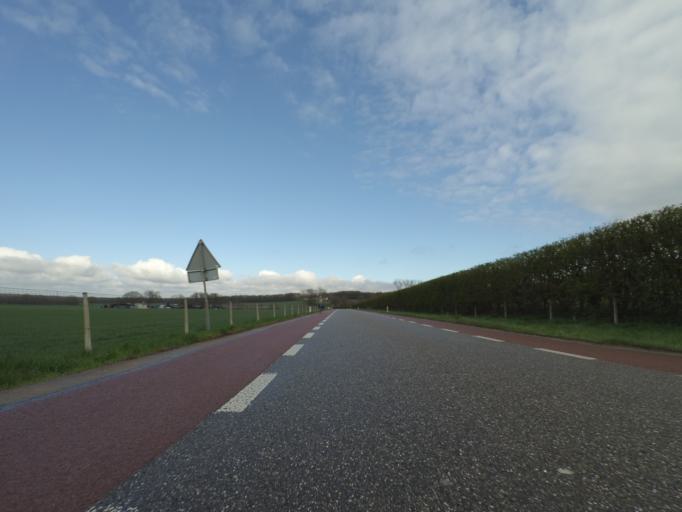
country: NL
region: Gelderland
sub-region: Gemeente Arnhem
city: Hoogkamp
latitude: 52.0635
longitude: 5.8951
